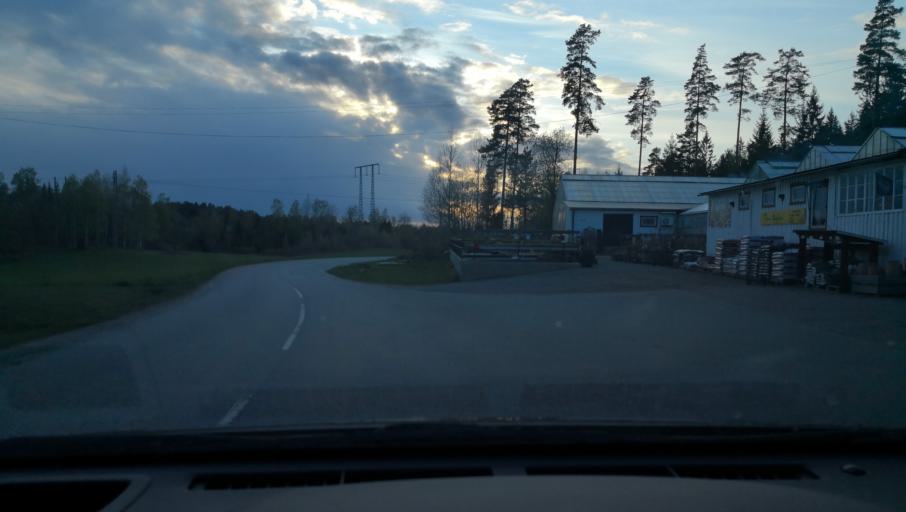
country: SE
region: OErebro
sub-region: Askersunds Kommun
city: Asbro
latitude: 58.9353
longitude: 15.0198
